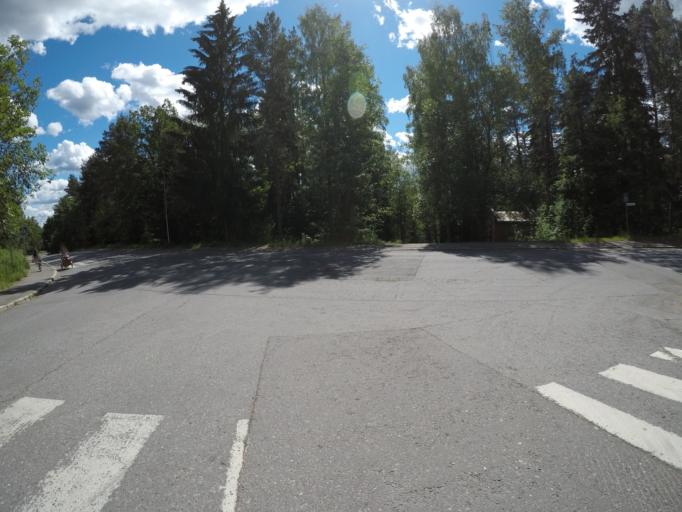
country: FI
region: Haeme
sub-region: Haemeenlinna
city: Haemeenlinna
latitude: 61.0125
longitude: 24.4407
